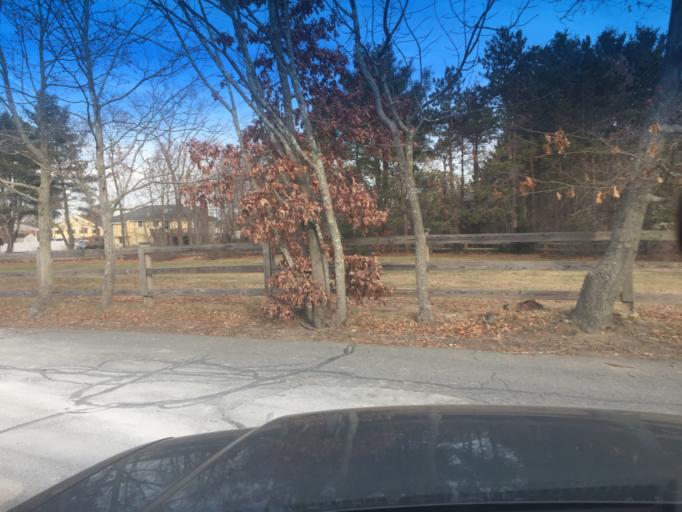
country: US
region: Massachusetts
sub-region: Norfolk County
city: Millis
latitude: 42.1659
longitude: -71.3579
